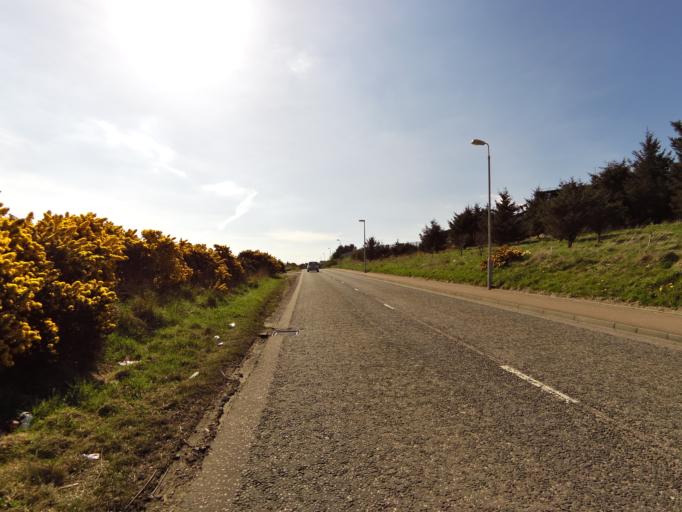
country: GB
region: Scotland
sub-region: Aberdeen City
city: Aberdeen
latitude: 57.1081
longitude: -2.0731
